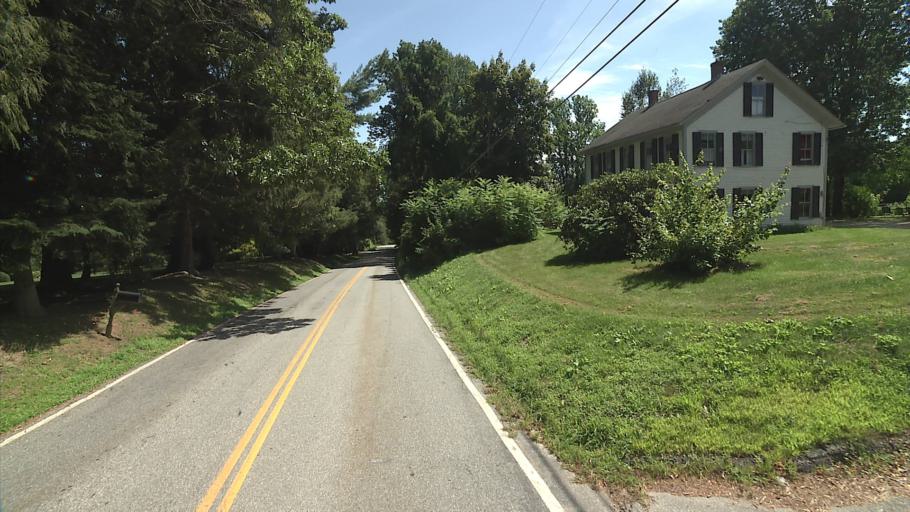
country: US
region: Connecticut
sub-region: Windham County
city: South Woodstock
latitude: 41.8750
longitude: -71.9735
